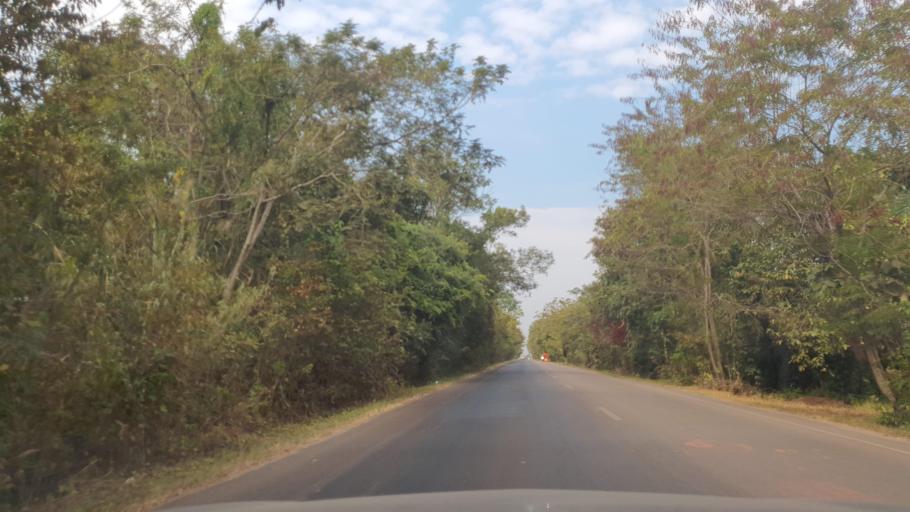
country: TH
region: Changwat Bueng Kan
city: Si Wilai
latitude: 18.2892
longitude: 103.8235
